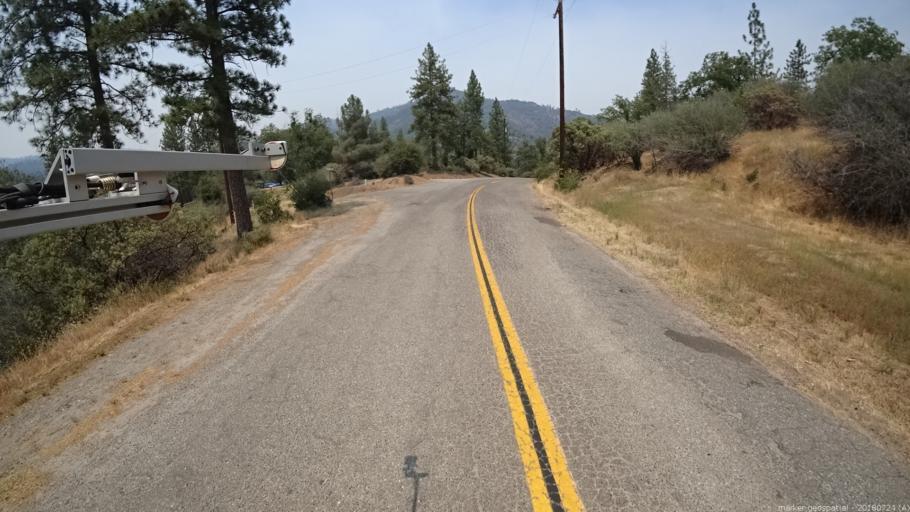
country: US
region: California
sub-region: Madera County
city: Oakhurst
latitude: 37.2463
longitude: -119.5576
